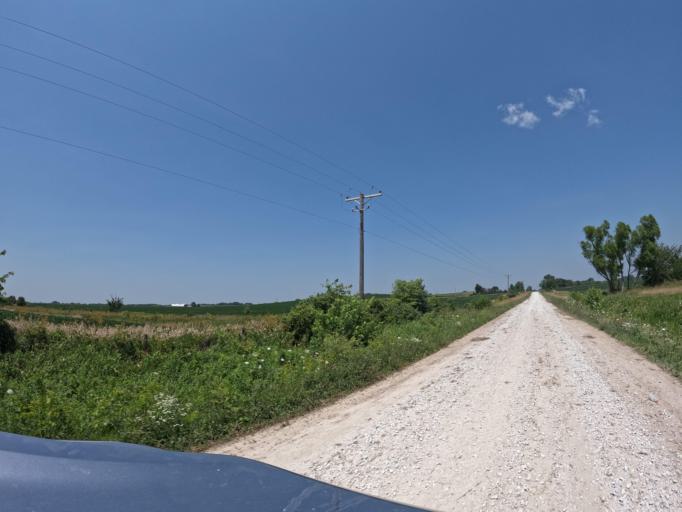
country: US
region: Iowa
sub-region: Keokuk County
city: Sigourney
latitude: 41.2913
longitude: -92.2095
